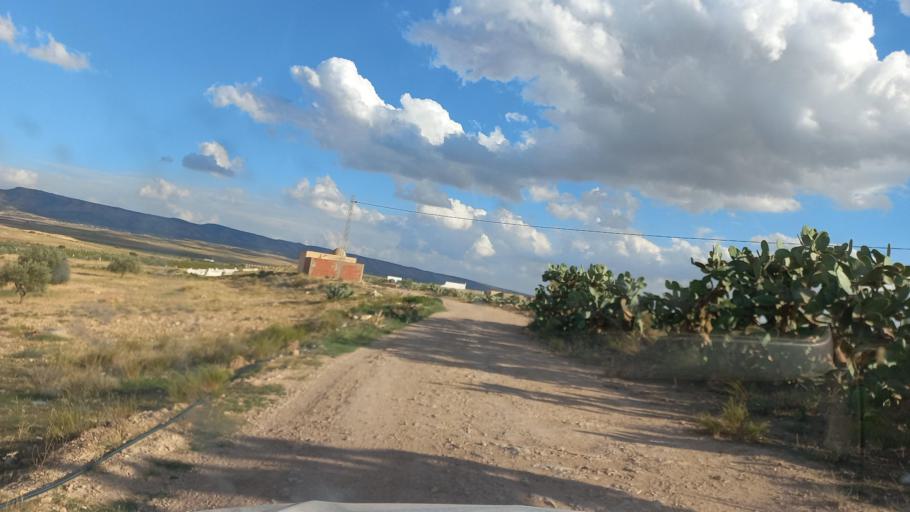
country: TN
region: Al Qasrayn
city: Sbiba
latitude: 35.3808
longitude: 9.0730
